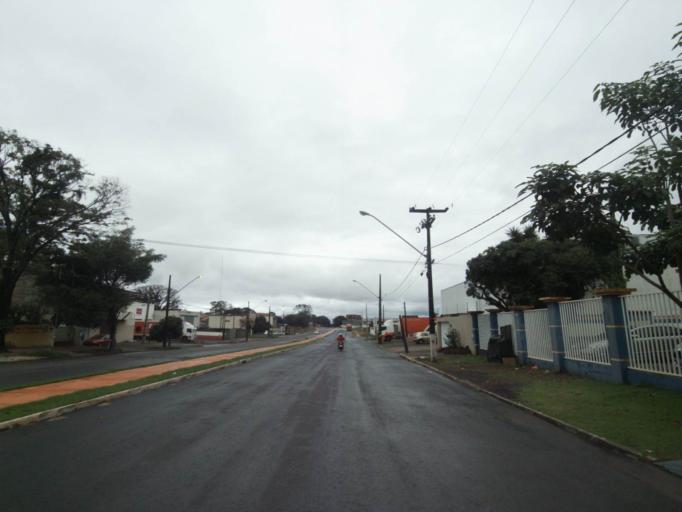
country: BR
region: Parana
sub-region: Foz Do Iguacu
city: Foz do Iguacu
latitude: -25.5143
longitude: -54.5613
